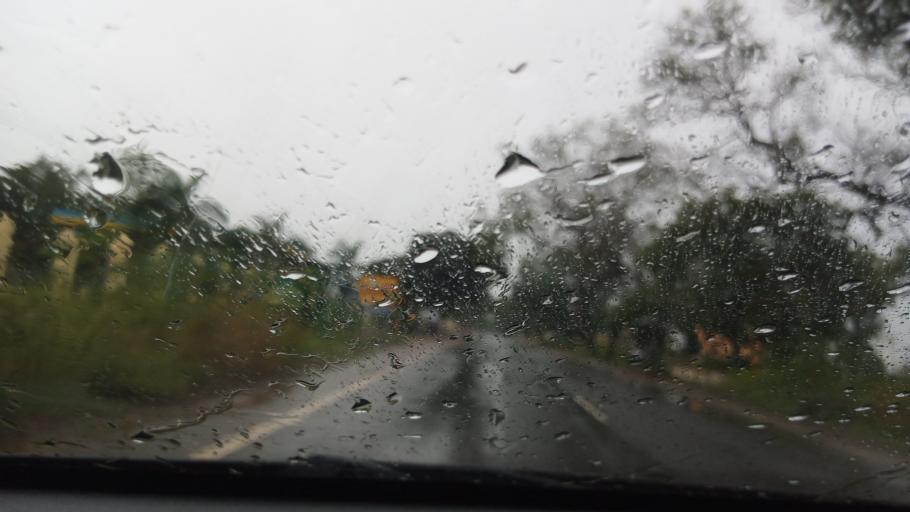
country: IN
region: Tamil Nadu
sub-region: Vellore
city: Kalavai
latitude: 12.8013
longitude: 79.4354
